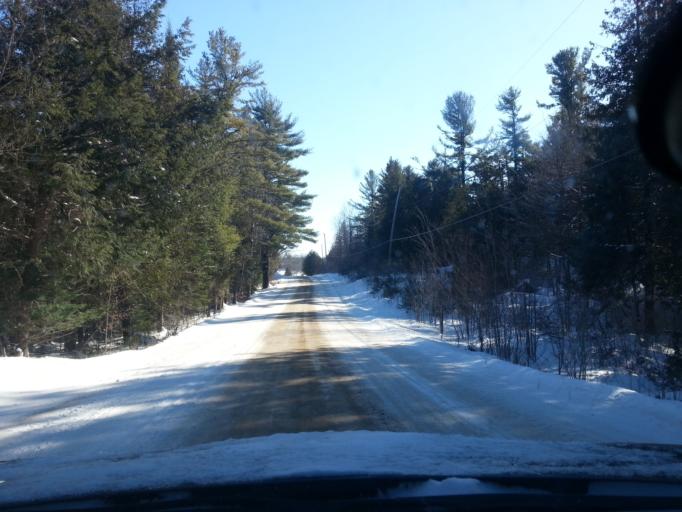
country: CA
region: Ontario
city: Arnprior
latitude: 45.2573
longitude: -76.3202
